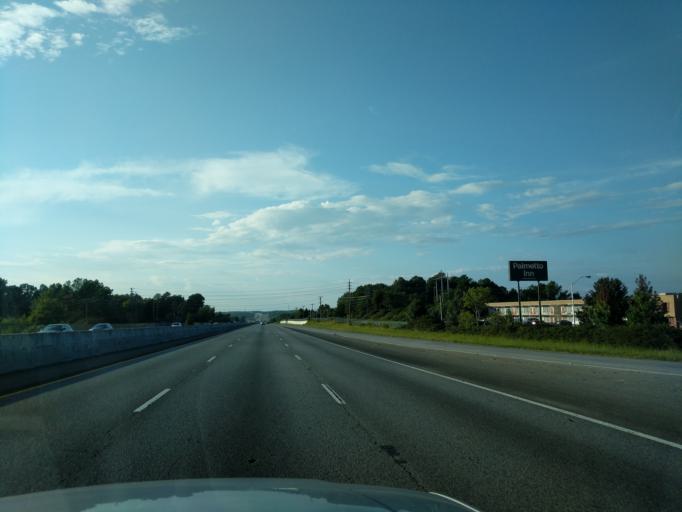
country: US
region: South Carolina
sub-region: Greenville County
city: Simpsonville
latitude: 34.7217
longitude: -82.2574
